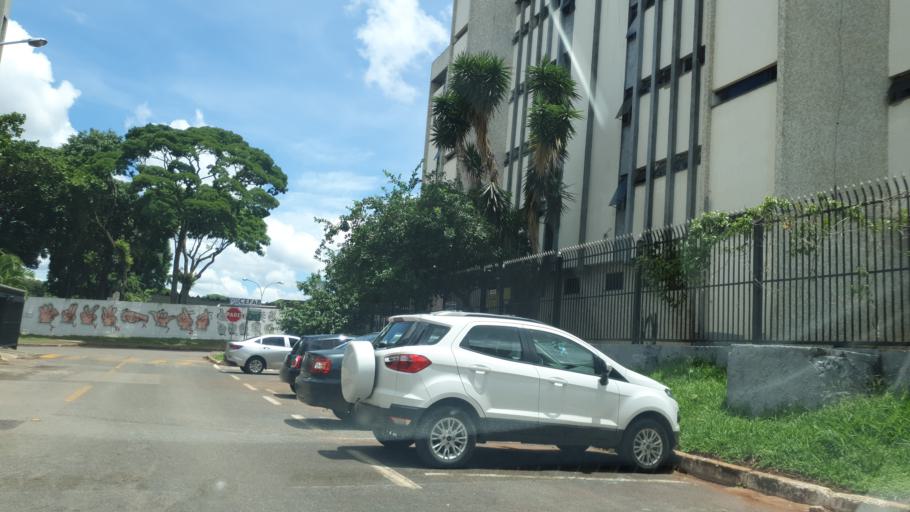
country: BR
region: Federal District
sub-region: Brasilia
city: Brasilia
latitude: -15.7943
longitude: -47.9420
